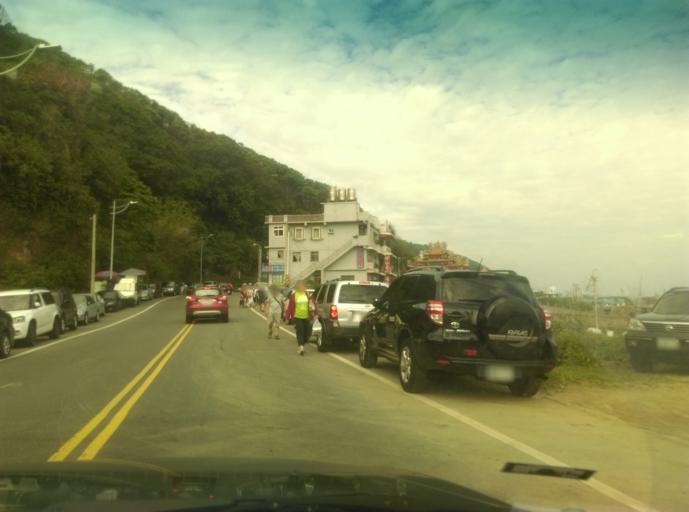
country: TW
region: Taiwan
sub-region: Keelung
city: Keelung
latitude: 25.1930
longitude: 121.6855
